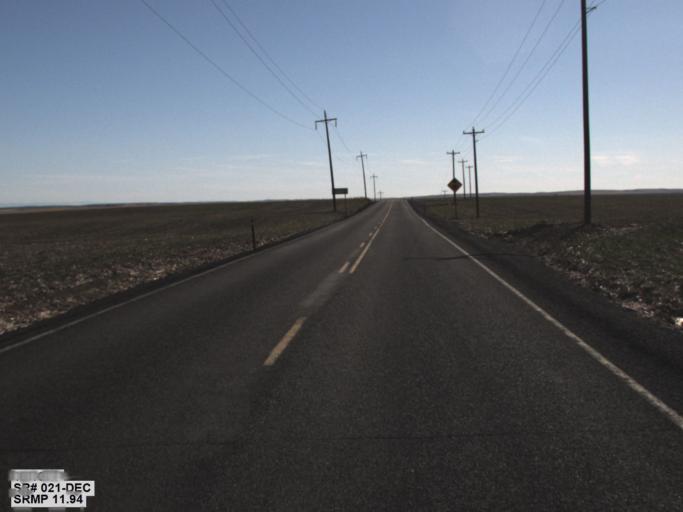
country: US
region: Washington
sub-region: Franklin County
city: Connell
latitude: 46.7992
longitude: -118.5473
